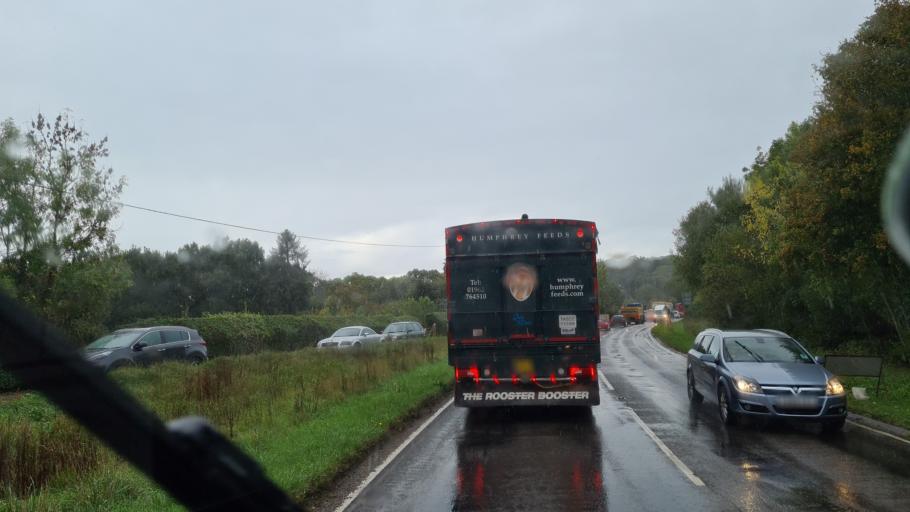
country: GB
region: England
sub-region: West Sussex
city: Washington
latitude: 50.9071
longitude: -0.4053
